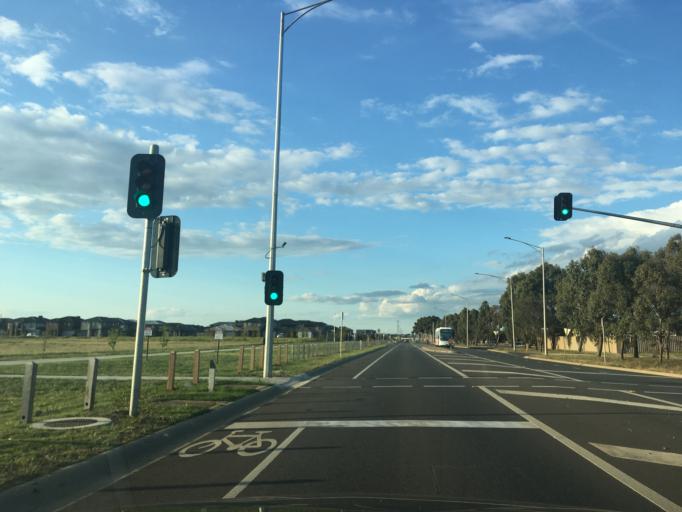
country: AU
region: Victoria
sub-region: Wyndham
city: Hoppers Crossing
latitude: -37.8890
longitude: 144.7180
